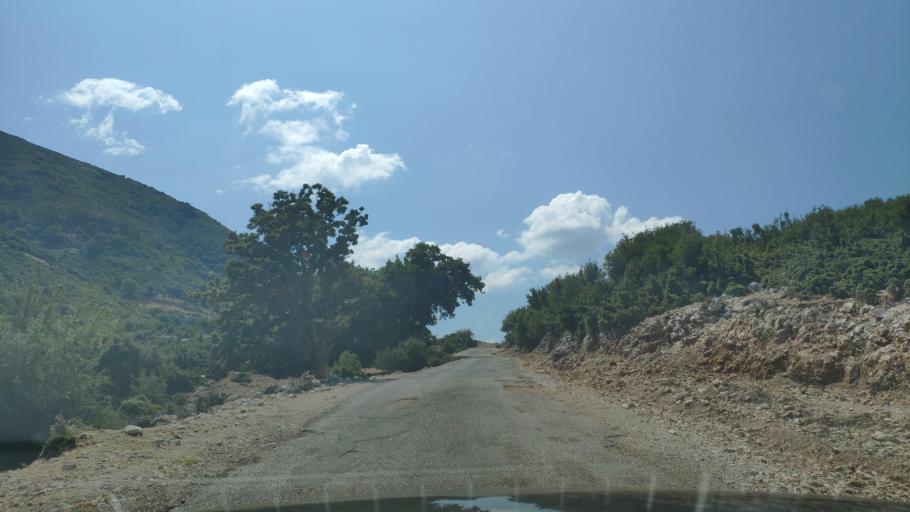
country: GR
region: West Greece
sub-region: Nomos Aitolias kai Akarnanias
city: Monastirakion
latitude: 38.8188
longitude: 20.9335
